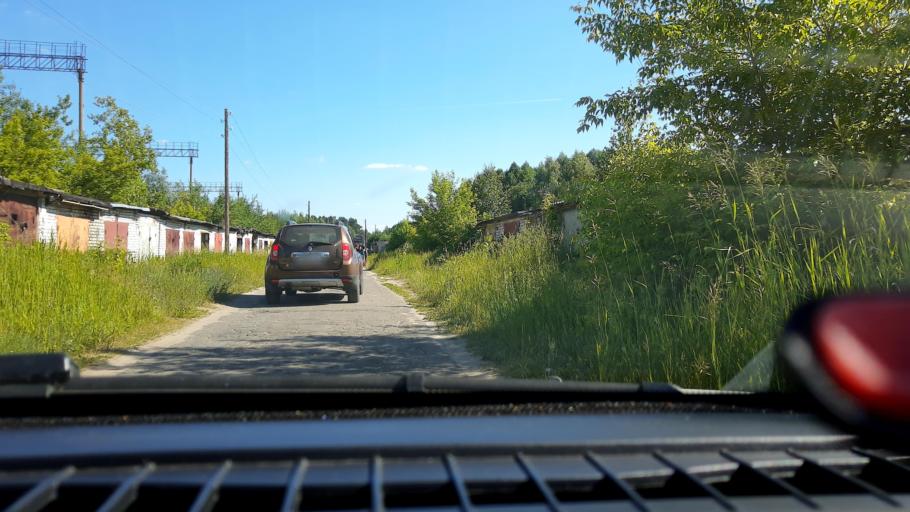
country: RU
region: Nizjnij Novgorod
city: Gidrotorf
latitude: 56.5093
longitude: 43.5358
